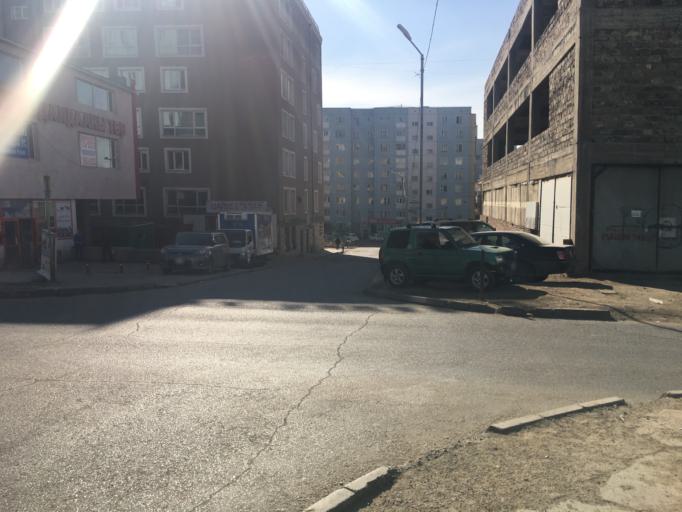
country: MN
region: Ulaanbaatar
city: Ulaanbaatar
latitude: 47.9221
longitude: 106.8816
